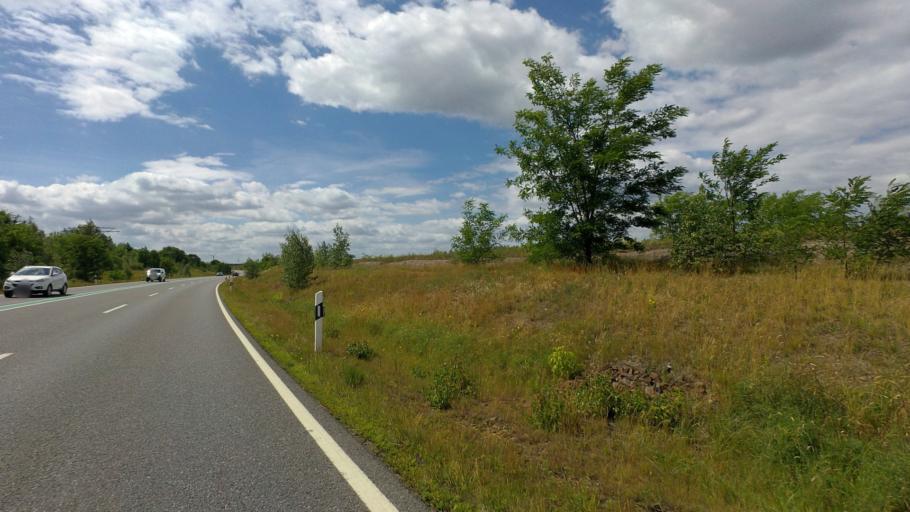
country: DE
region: Brandenburg
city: Senftenberg
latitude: 51.5347
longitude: 14.0033
